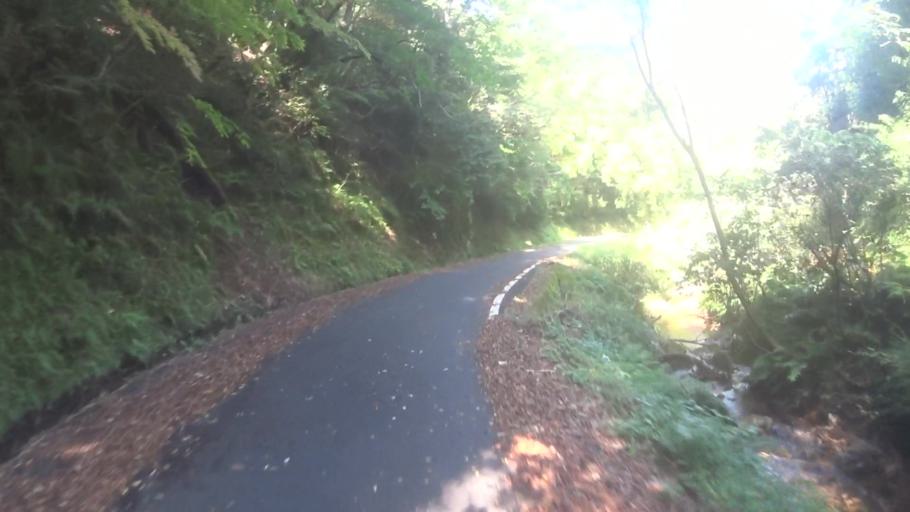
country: JP
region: Kyoto
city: Miyazu
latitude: 35.6947
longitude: 135.1346
